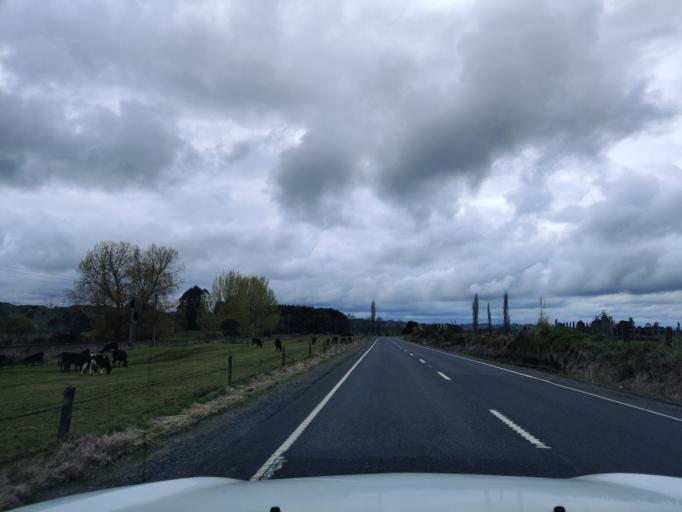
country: NZ
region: Waikato
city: Turangi
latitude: -39.0249
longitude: 175.3813
